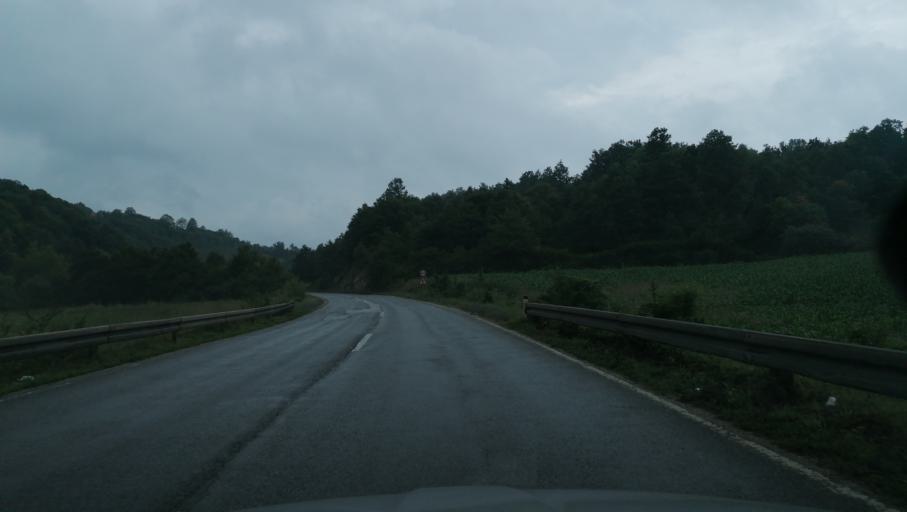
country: RS
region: Central Serbia
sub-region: Zlatiborski Okrug
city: Cajetina
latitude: 43.7890
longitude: 19.7179
